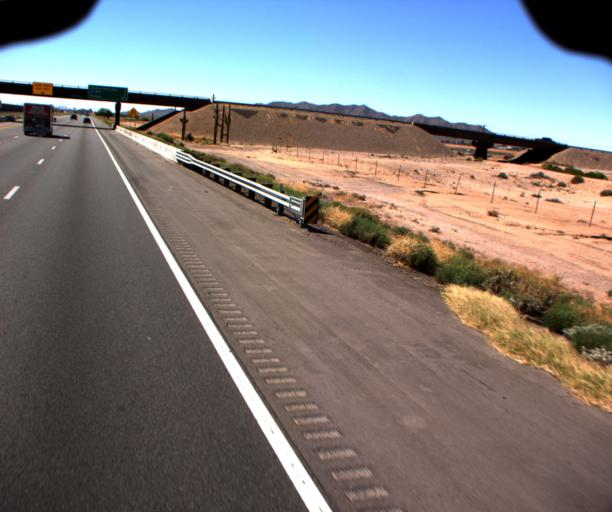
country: US
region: Arizona
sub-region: Pinal County
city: Casa Grande
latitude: 32.8662
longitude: -111.6872
